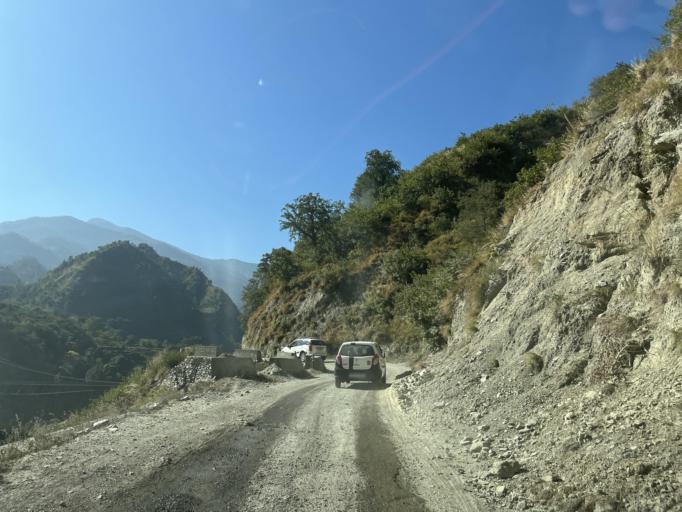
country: IN
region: Uttarakhand
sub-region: Naini Tal
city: Naini Tal
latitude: 29.5098
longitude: 79.4500
